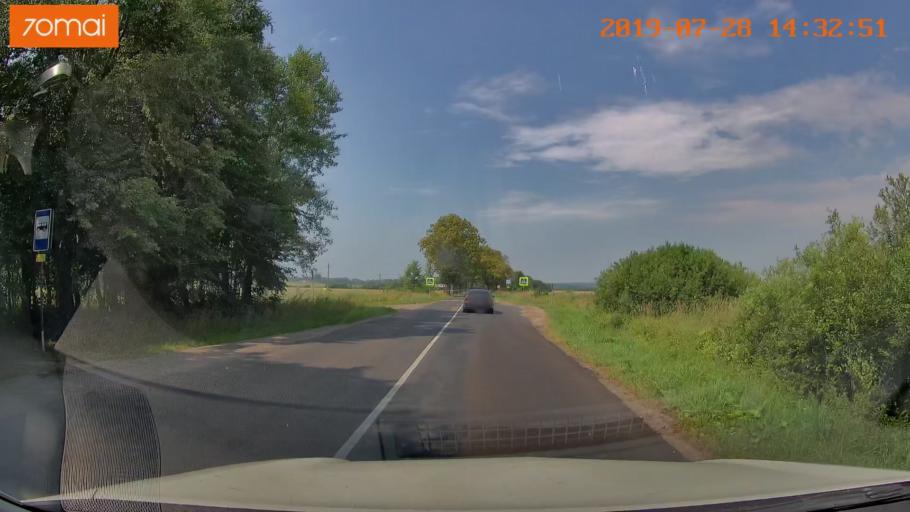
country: RU
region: Kaliningrad
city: Primorsk
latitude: 54.8155
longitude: 20.0374
